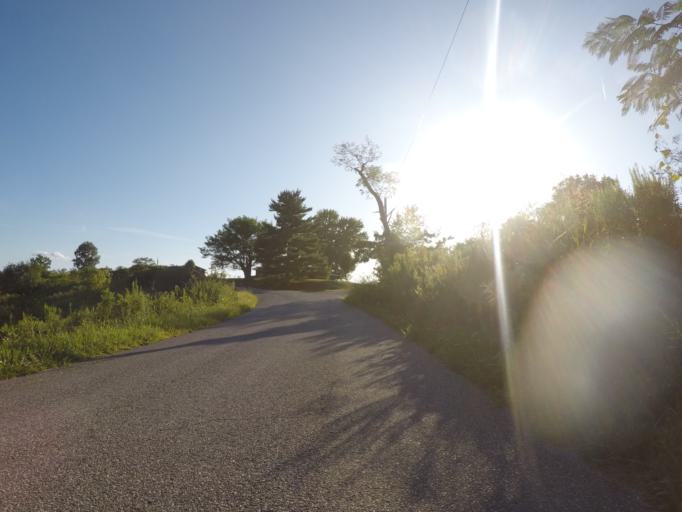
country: US
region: Ohio
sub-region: Lawrence County
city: Burlington
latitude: 38.5279
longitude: -82.5249
